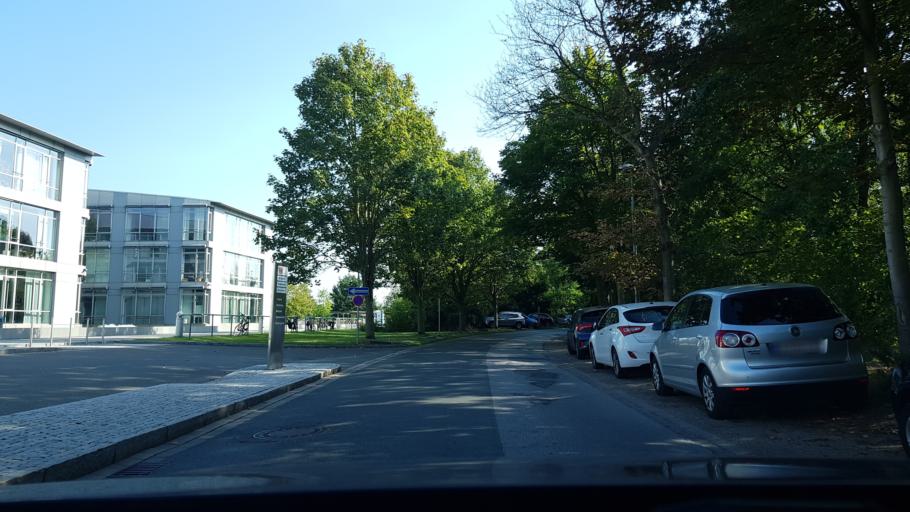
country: DE
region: North Rhine-Westphalia
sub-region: Regierungsbezirk Dusseldorf
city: Duisburg
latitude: 51.4088
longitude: 6.7950
